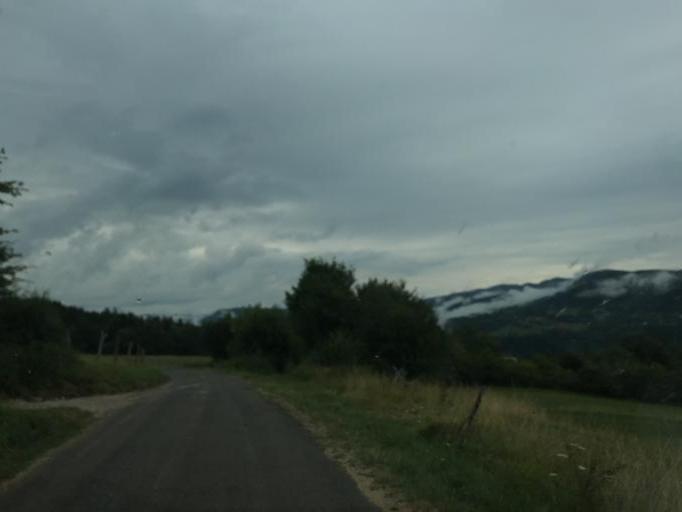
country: FR
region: Franche-Comte
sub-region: Departement du Jura
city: Lavans-les-Saint-Claude
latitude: 46.3314
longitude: 5.7542
